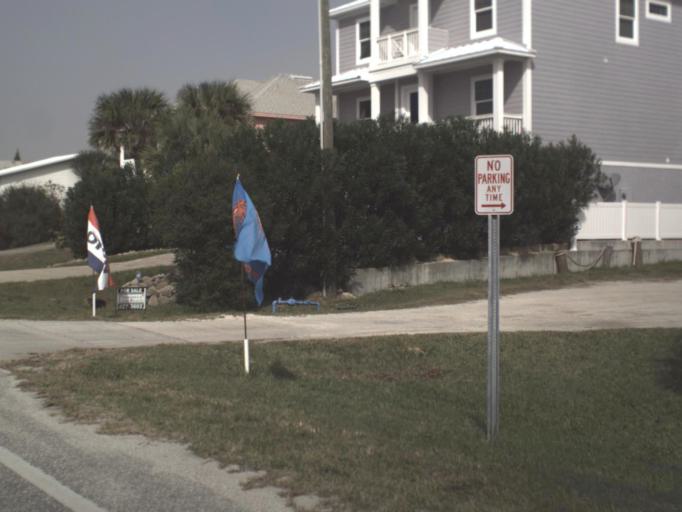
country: US
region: Florida
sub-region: Volusia County
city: Edgewater
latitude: 28.9541
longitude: -80.8425
